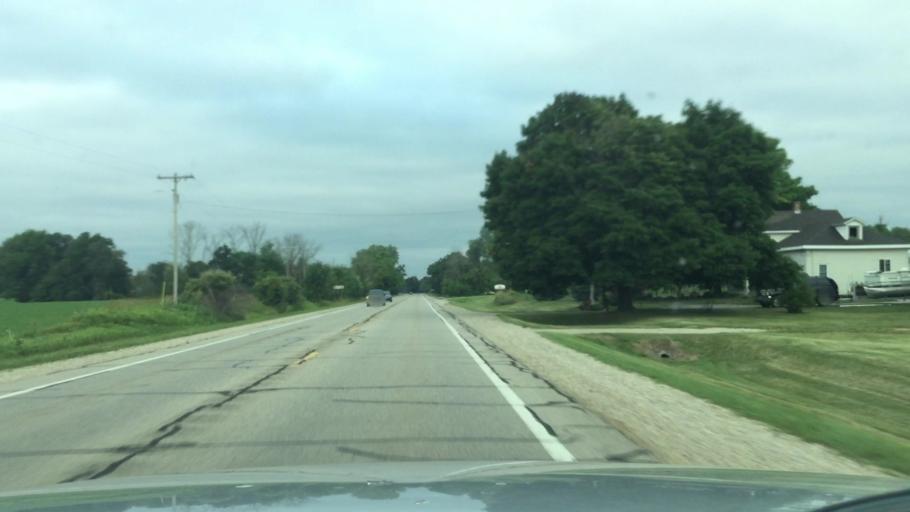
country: US
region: Michigan
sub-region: Montcalm County
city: Stanton
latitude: 43.1780
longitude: -85.0943
